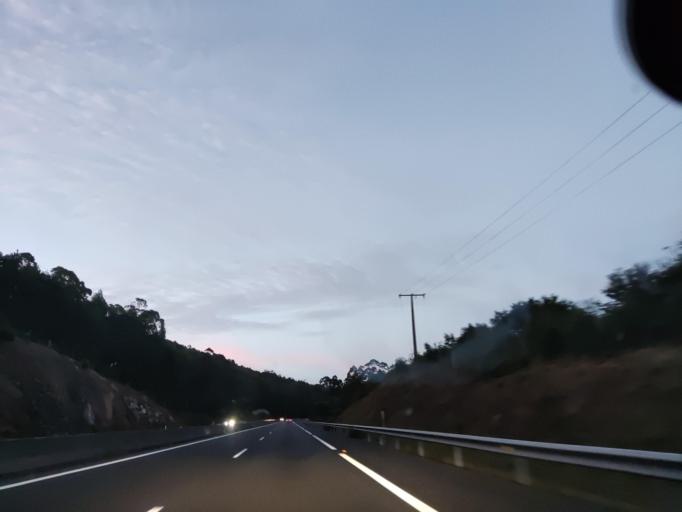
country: ES
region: Galicia
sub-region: Provincia da Coruna
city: Boiro
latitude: 42.6168
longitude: -8.9526
